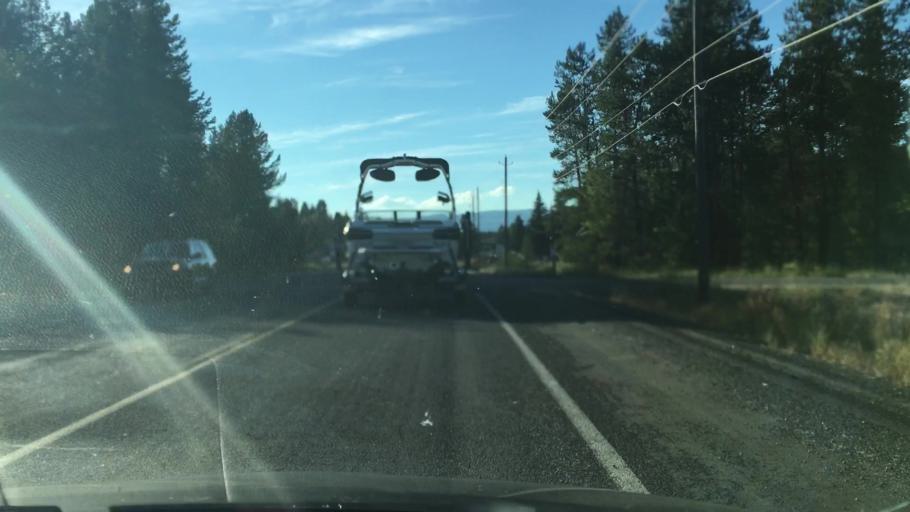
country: US
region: Idaho
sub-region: Valley County
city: Cascade
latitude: 44.5029
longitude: -116.0265
